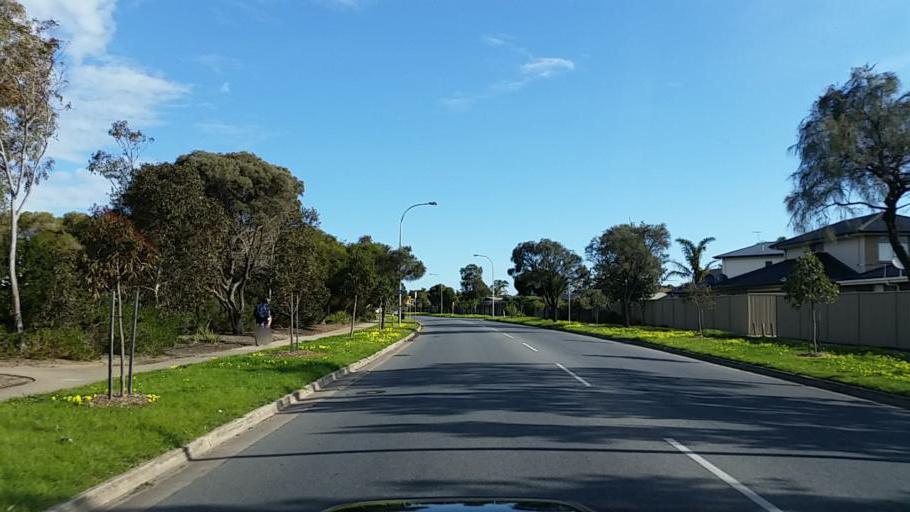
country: AU
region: South Australia
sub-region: Charles Sturt
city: West Lakes Shore
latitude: -34.8659
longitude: 138.4848
